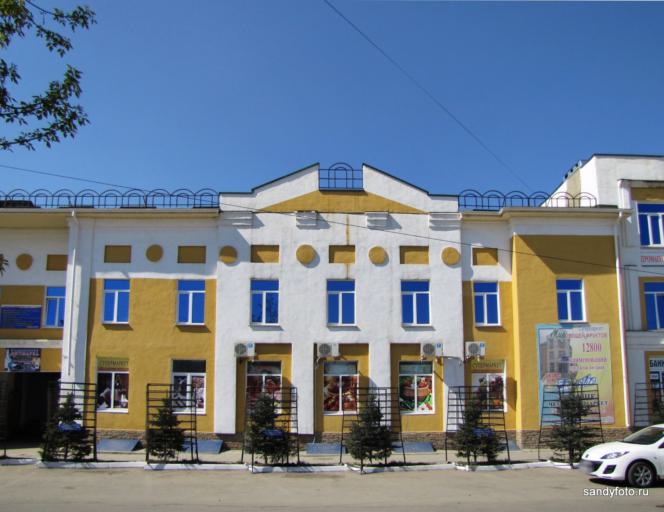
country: RU
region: Chelyabinsk
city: Troitsk
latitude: 54.0850
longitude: 61.5585
